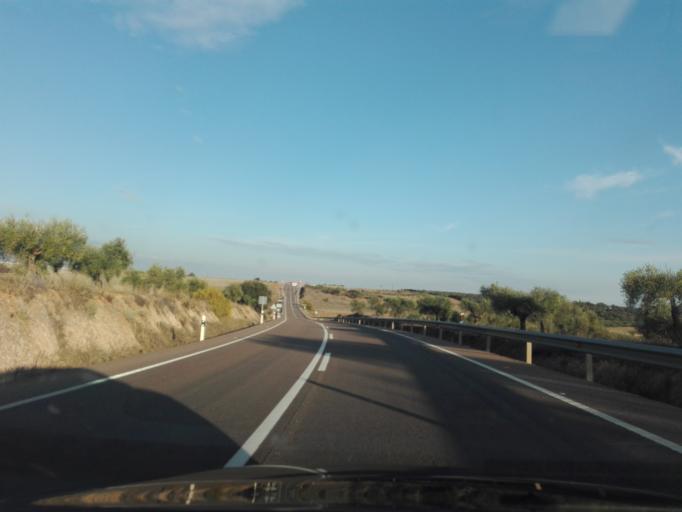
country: ES
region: Extremadura
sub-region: Provincia de Badajoz
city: Usagre
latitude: 38.3446
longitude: -6.1814
